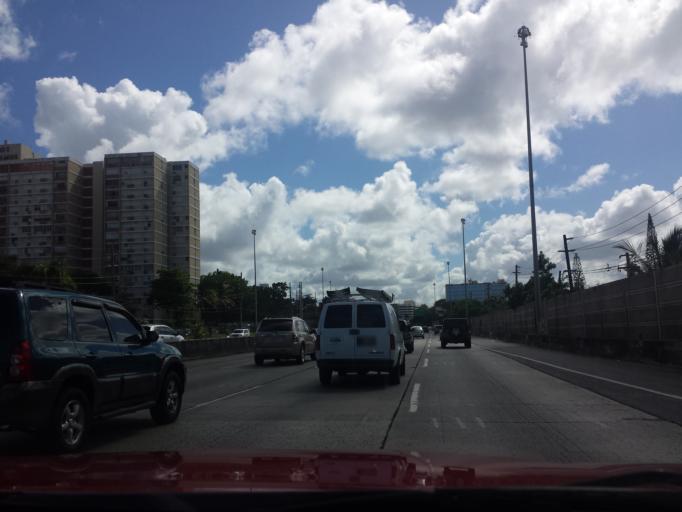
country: PR
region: Catano
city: Catano
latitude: 18.4045
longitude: -66.0704
